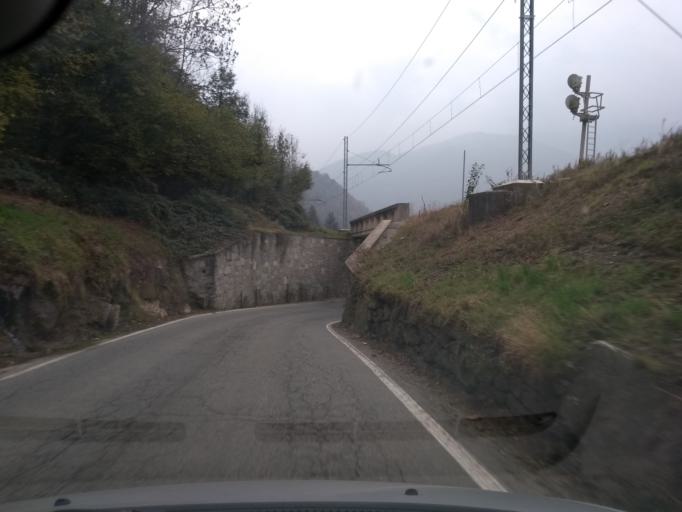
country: IT
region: Piedmont
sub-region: Provincia di Torino
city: Mezzenile
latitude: 45.3014
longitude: 7.3991
